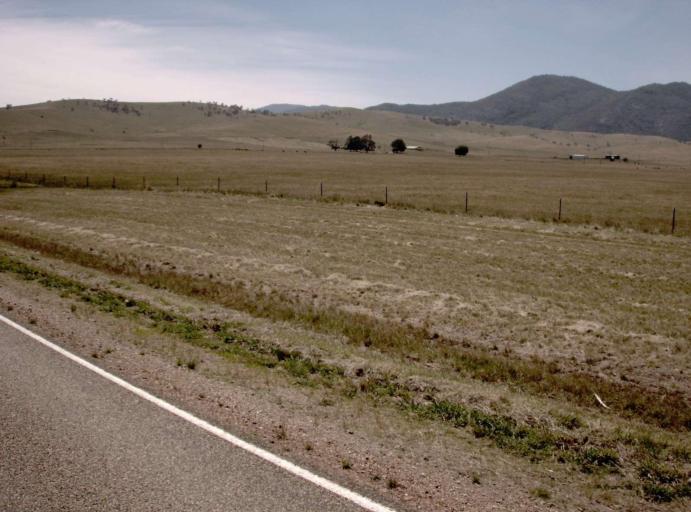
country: AU
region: Victoria
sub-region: Alpine
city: Mount Beauty
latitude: -36.9996
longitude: 147.6740
